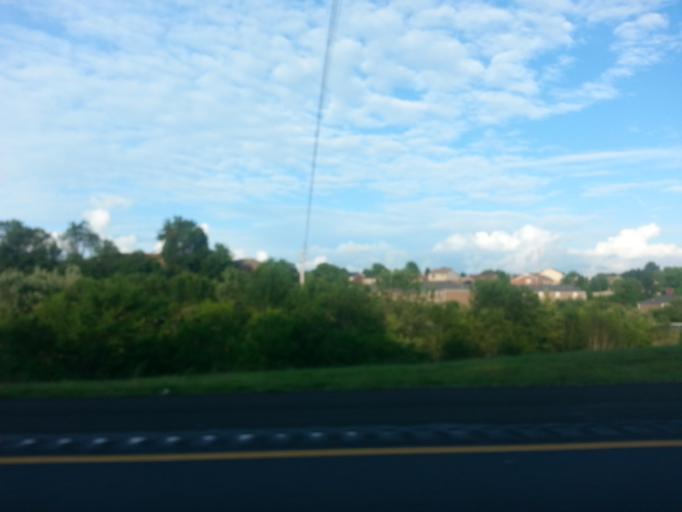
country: US
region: Kentucky
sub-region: Madison County
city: Richmond
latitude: 37.7286
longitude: -84.3236
